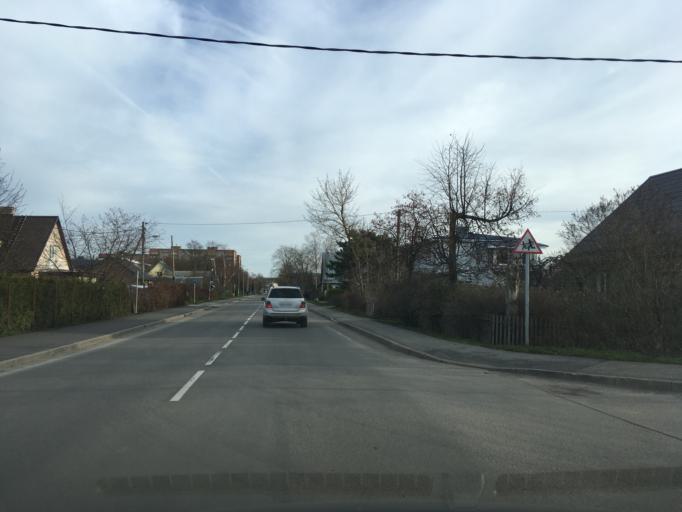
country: EE
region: Ida-Virumaa
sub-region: Narva linn
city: Narva
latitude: 59.3635
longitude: 28.1770
